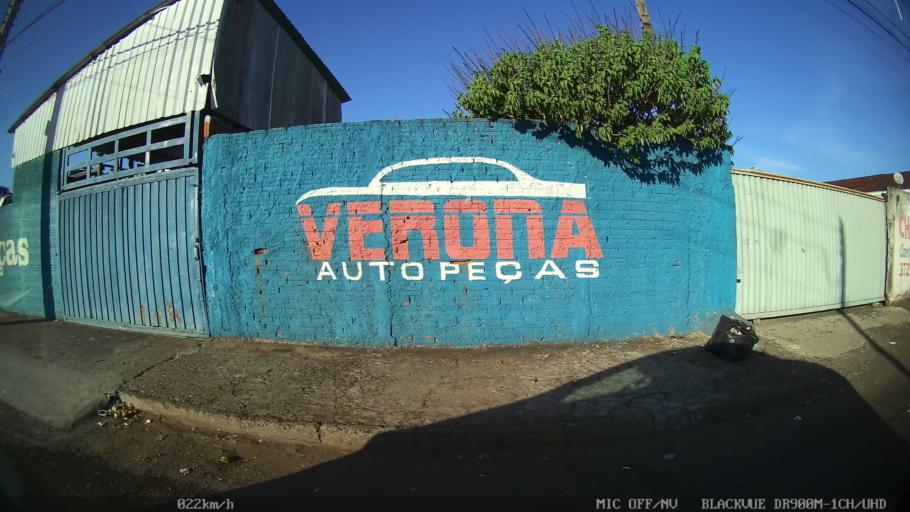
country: BR
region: Sao Paulo
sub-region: Franca
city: Franca
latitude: -20.5269
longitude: -47.3777
